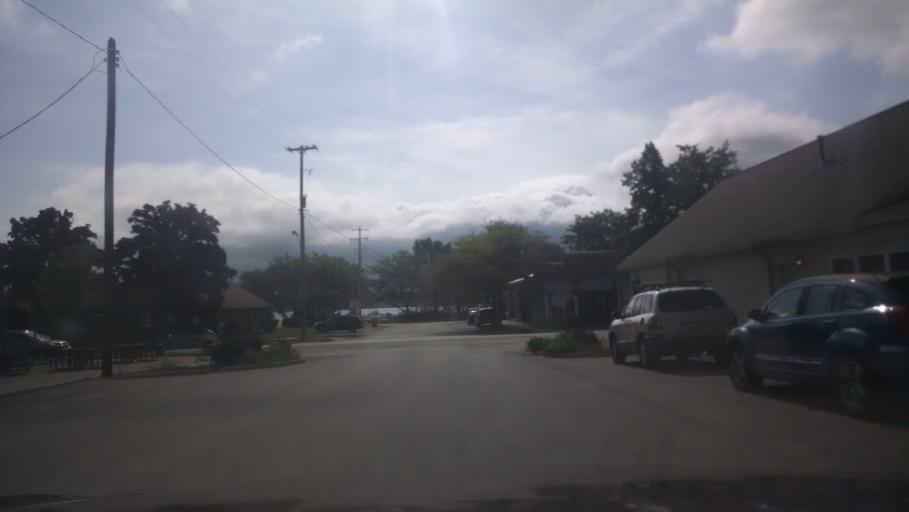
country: US
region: Michigan
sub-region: Leelanau County
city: Leland
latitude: 44.9780
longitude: -85.6507
